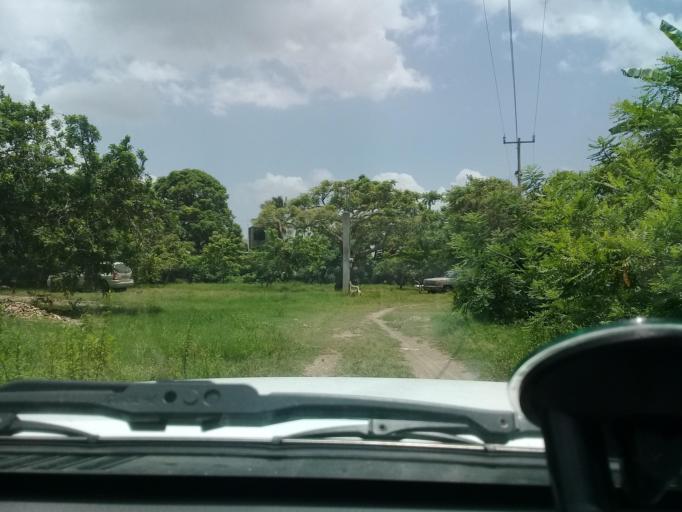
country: MX
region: Veracruz
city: Moralillo
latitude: 22.1382
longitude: -98.0402
